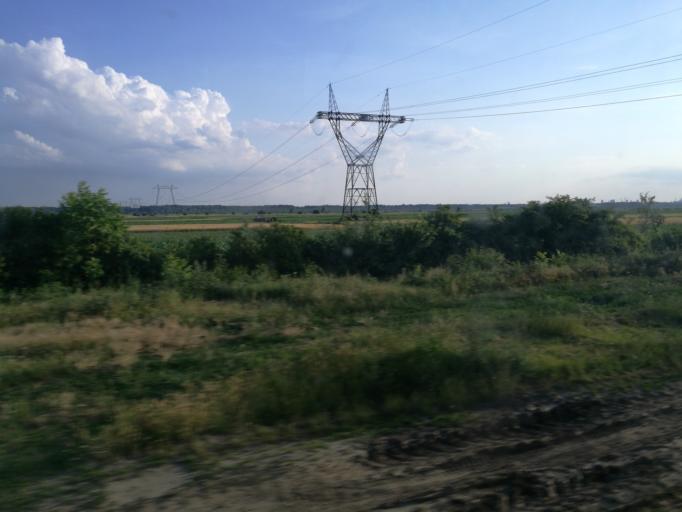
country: RO
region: Arges
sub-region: Comuna Calinesti
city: Calinesti
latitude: 44.8185
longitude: 25.0374
